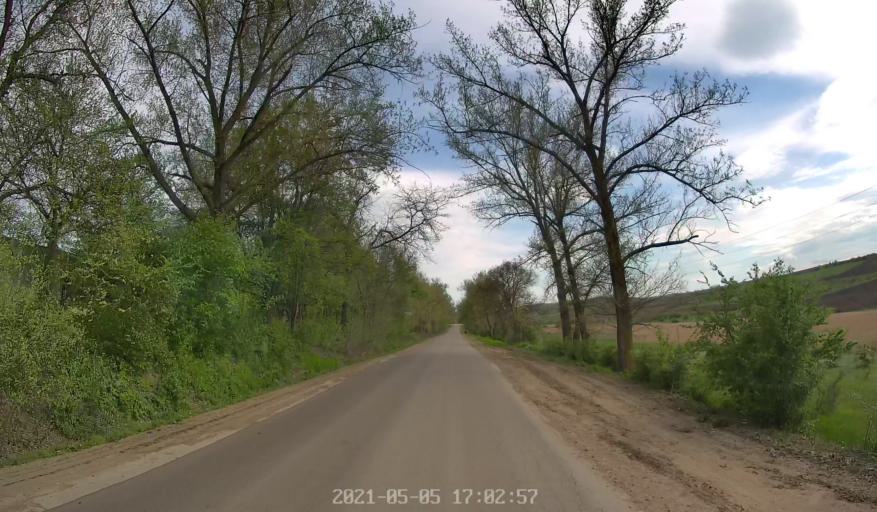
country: MD
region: Chisinau
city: Vadul lui Voda
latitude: 47.0557
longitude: 29.1325
